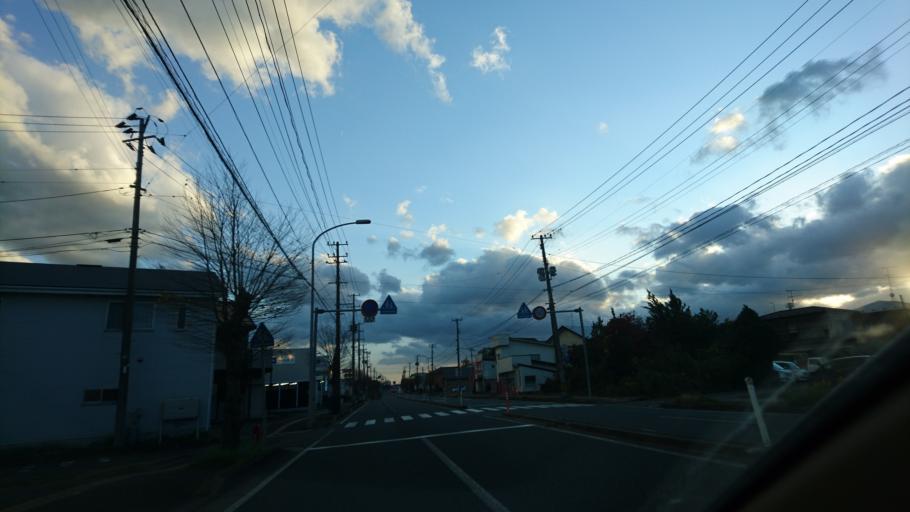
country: JP
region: Iwate
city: Mizusawa
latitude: 39.1501
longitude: 141.1324
